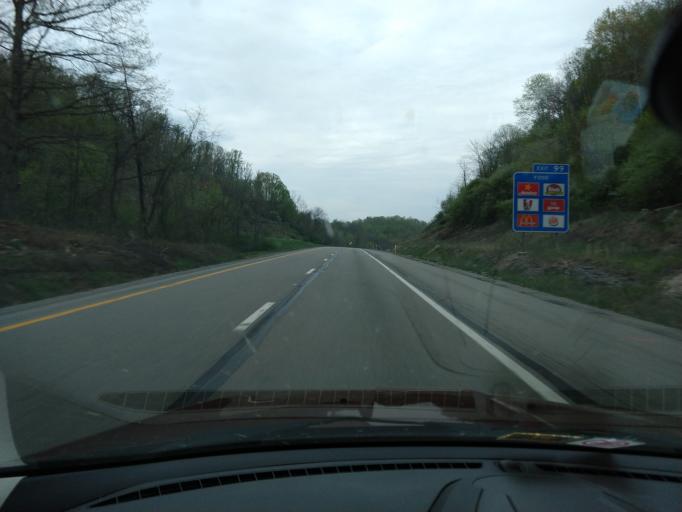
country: US
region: West Virginia
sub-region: Lewis County
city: Weston
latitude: 39.0151
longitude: -80.4489
